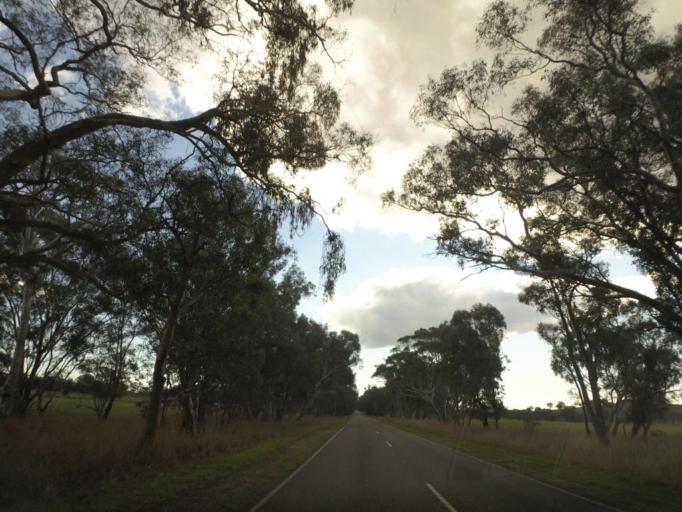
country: AU
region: New South Wales
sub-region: Corowa Shire
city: Howlong
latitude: -36.1912
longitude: 146.6143
